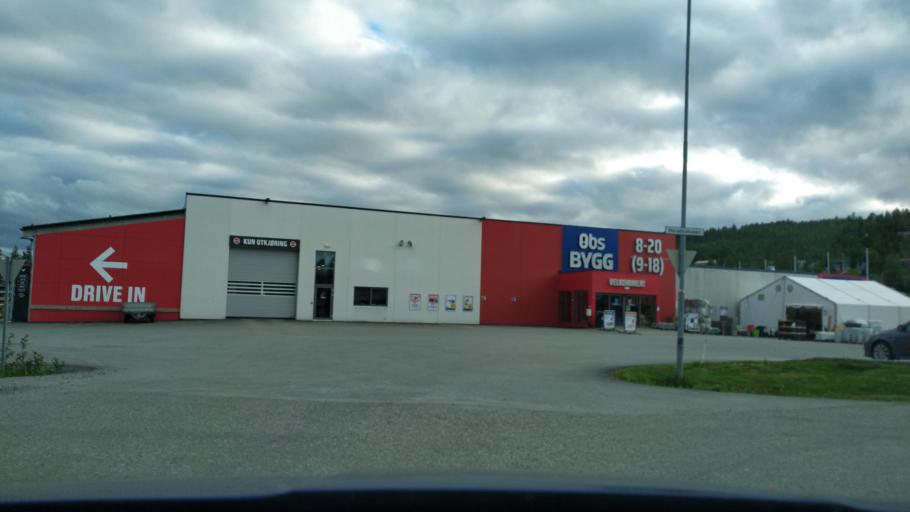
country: NO
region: Troms
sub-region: Malselv
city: Moen
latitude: 69.0904
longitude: 18.5860
